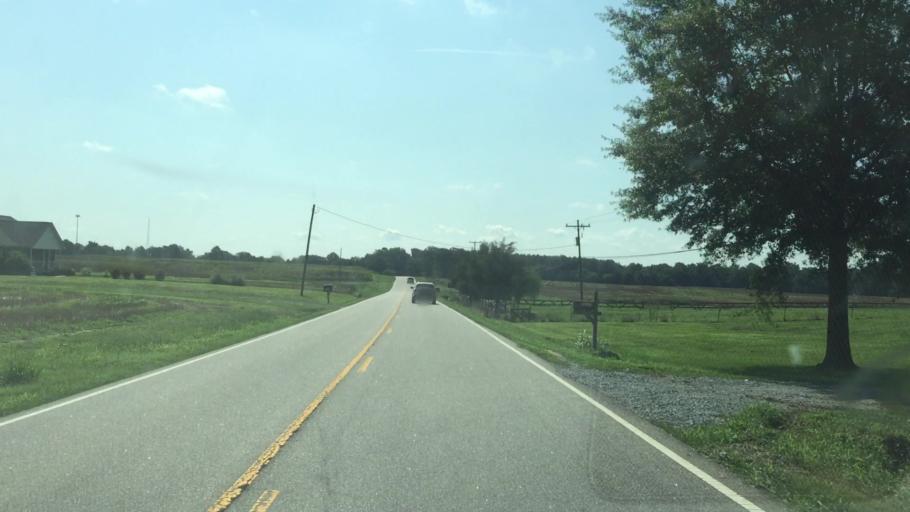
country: US
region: North Carolina
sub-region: Stanly County
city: Oakboro
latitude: 35.1268
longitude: -80.3607
